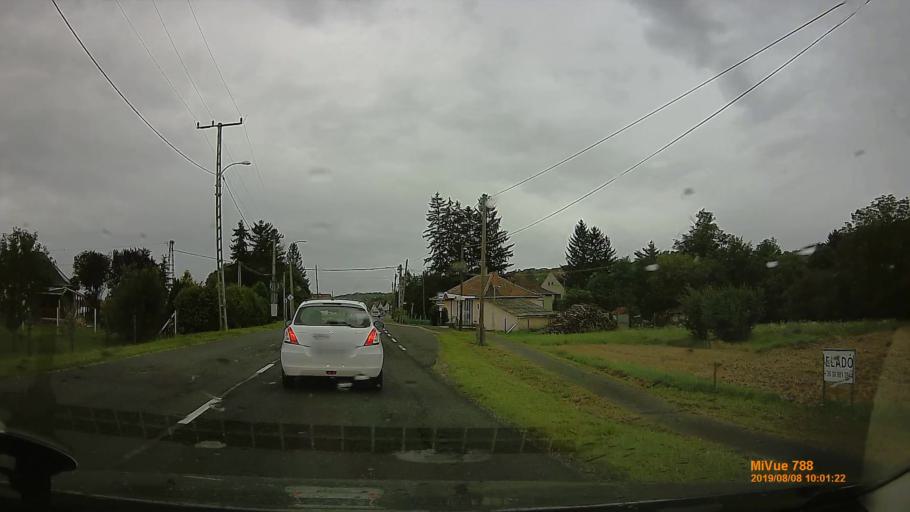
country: HU
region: Zala
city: Zalaegerszeg
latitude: 46.9442
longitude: 16.8495
